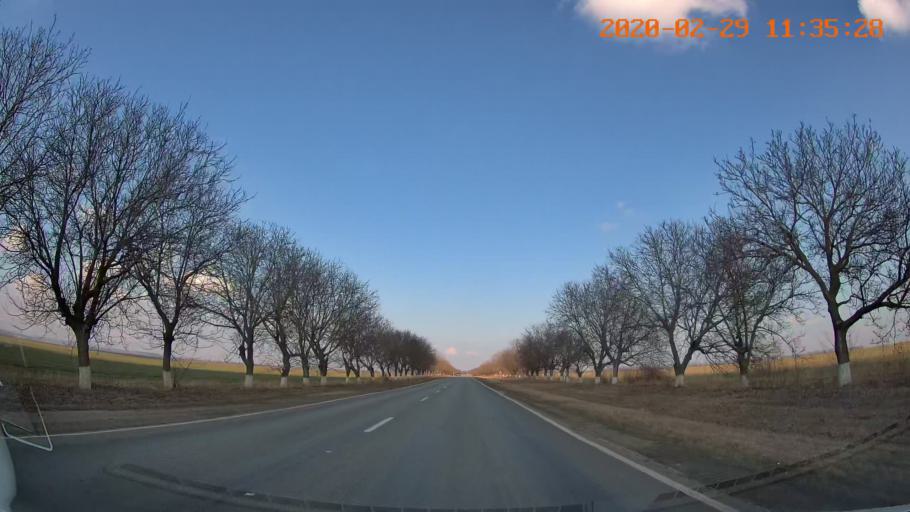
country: MD
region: Rezina
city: Saharna
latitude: 47.5810
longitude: 29.0631
